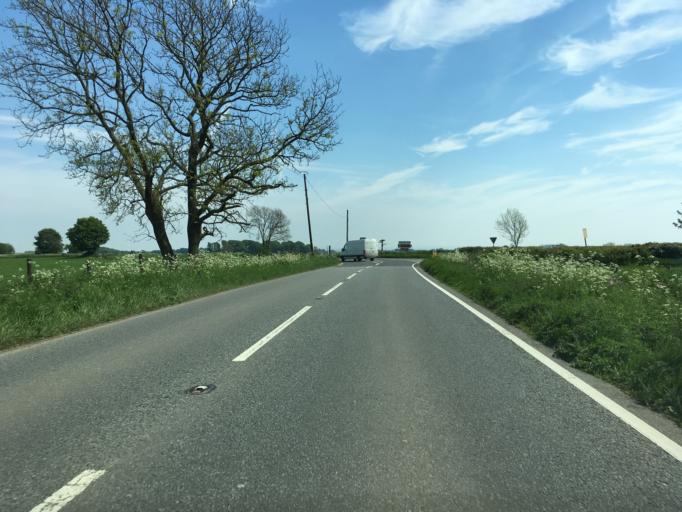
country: GB
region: England
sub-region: Gloucestershire
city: Dursley
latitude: 51.6663
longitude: -2.3030
